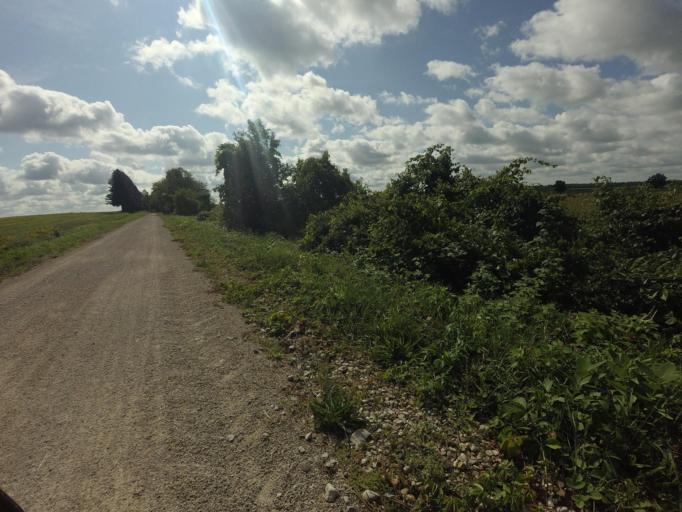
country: CA
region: Ontario
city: Huron East
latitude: 43.7111
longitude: -81.3745
